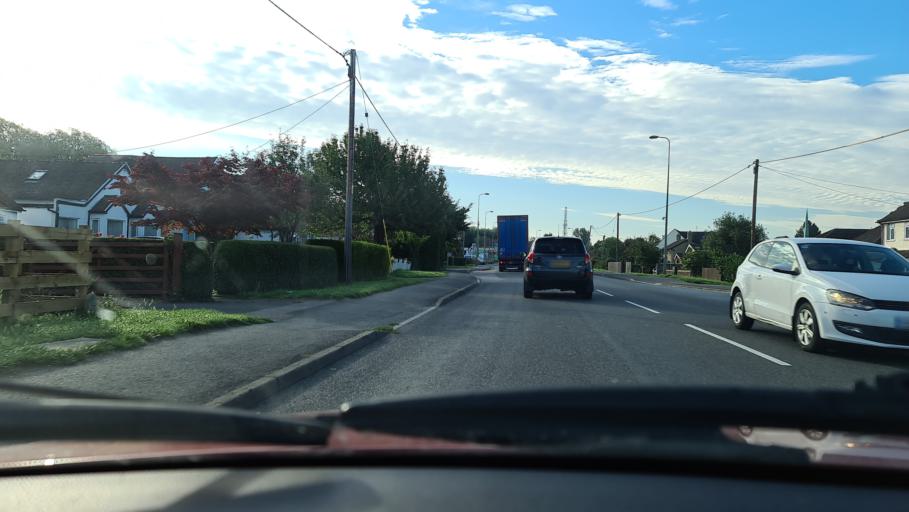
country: GB
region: England
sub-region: Oxfordshire
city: Kidlington
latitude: 51.8186
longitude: -1.2837
